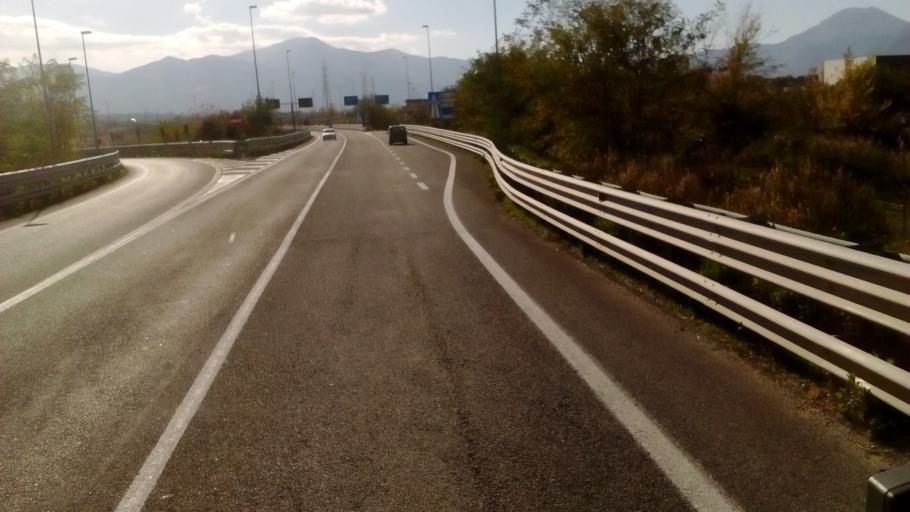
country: IT
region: Molise
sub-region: Provincia di Isernia
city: Taverna Ravindola
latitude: 41.5108
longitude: 14.1151
